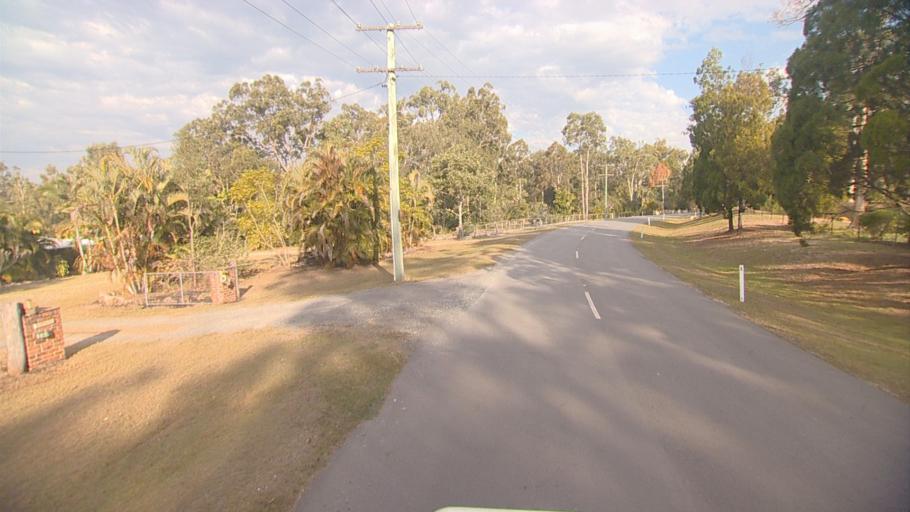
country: AU
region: Queensland
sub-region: Logan
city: Chambers Flat
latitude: -27.7797
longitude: 153.1089
